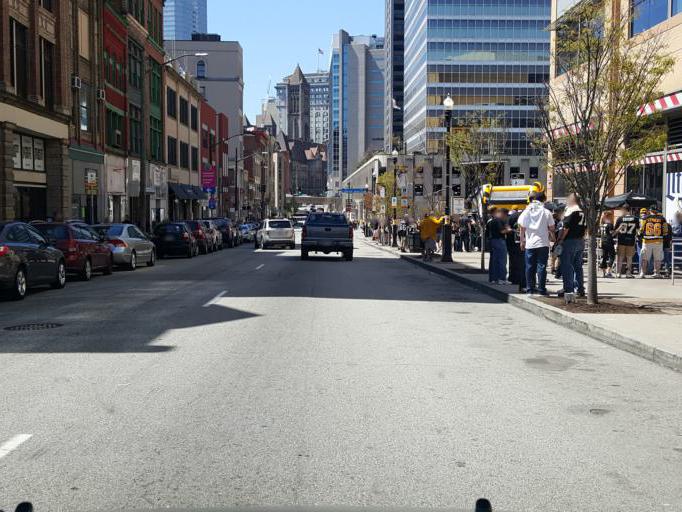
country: US
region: Pennsylvania
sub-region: Allegheny County
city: Pittsburgh
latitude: 40.4388
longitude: -79.9895
